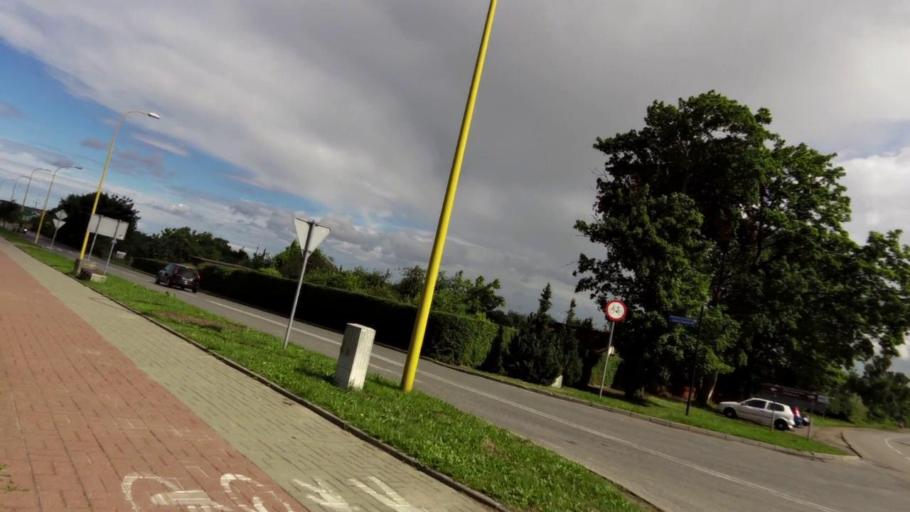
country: PL
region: West Pomeranian Voivodeship
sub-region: Powiat slawienski
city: Darlowo
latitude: 54.4266
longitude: 16.4169
